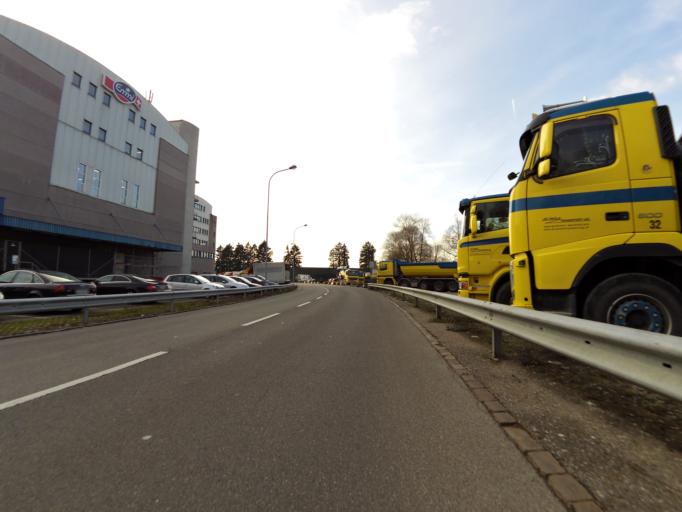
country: CH
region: Zurich
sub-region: Bezirk Dietikon
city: Oberengstringen / Zentrum
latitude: 47.4039
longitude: 8.4612
